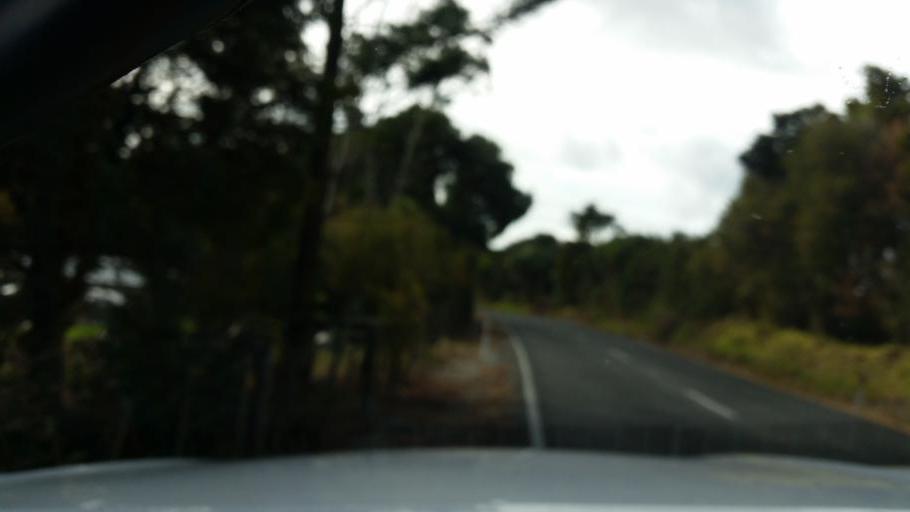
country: NZ
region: Auckland
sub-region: Auckland
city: Wellsford
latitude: -36.0863
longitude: 174.5471
